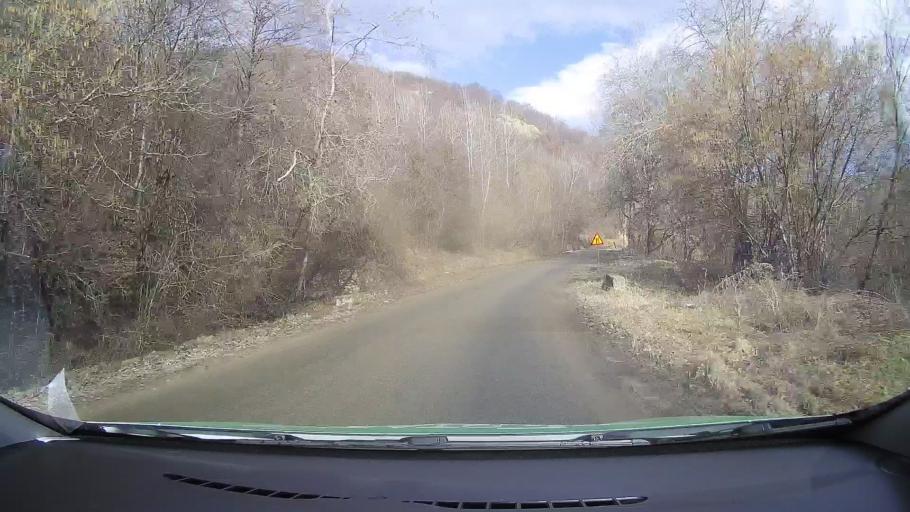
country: RO
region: Dambovita
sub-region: Comuna Motaeni
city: Motaeni
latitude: 45.1016
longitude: 25.4405
